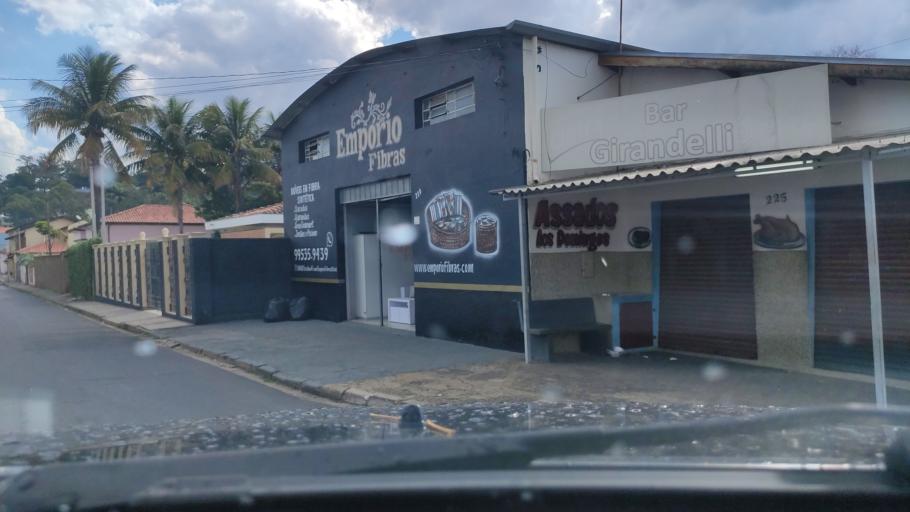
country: BR
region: Sao Paulo
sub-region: Itapira
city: Itapira
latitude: -22.4375
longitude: -46.8164
